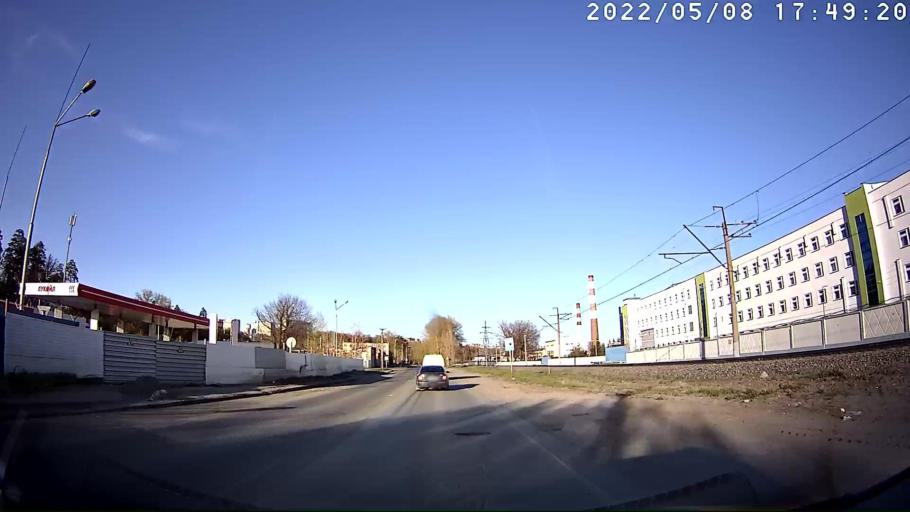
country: RU
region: Tatarstan
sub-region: Zelenodol'skiy Rayon
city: Zelenodolsk
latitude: 55.8413
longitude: 48.4760
